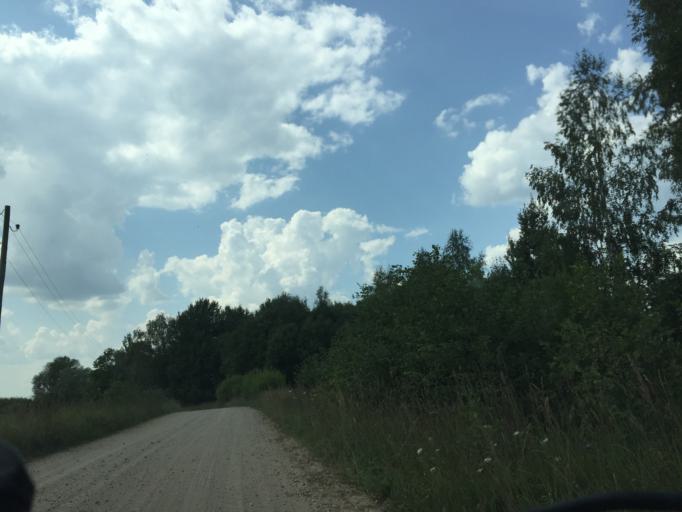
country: LT
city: Zagare
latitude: 56.3522
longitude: 23.1570
